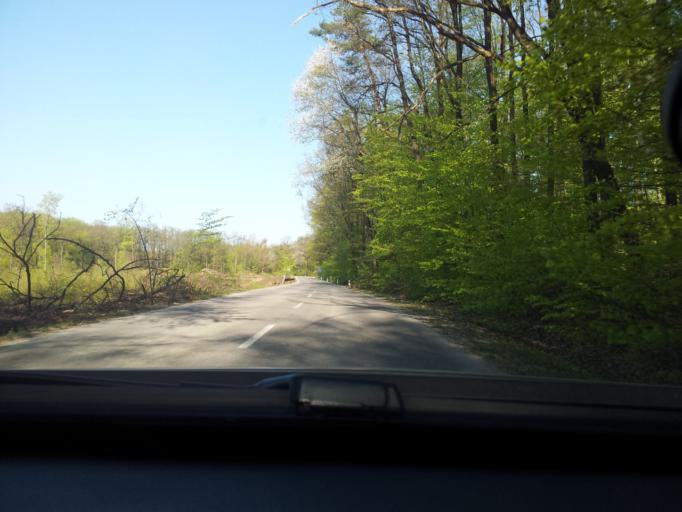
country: SK
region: Nitriansky
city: Partizanske
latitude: 48.5110
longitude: 18.4044
